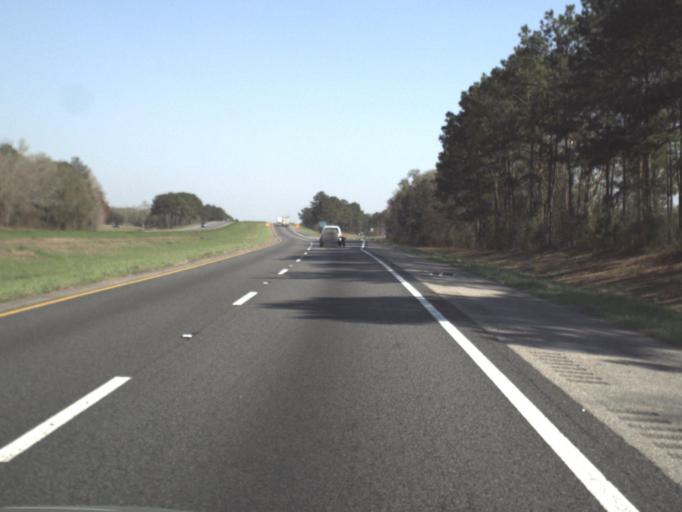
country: US
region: Florida
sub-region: Gadsden County
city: Gretna
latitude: 30.5801
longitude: -84.7066
